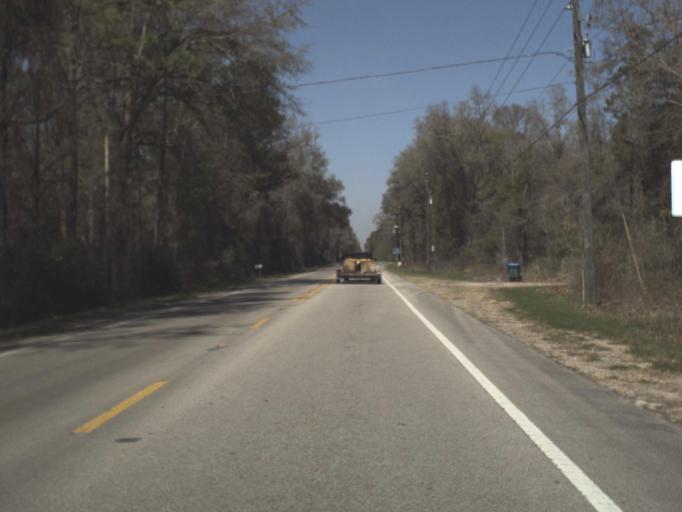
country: US
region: Florida
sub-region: Leon County
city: Woodville
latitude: 30.2659
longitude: -84.2372
